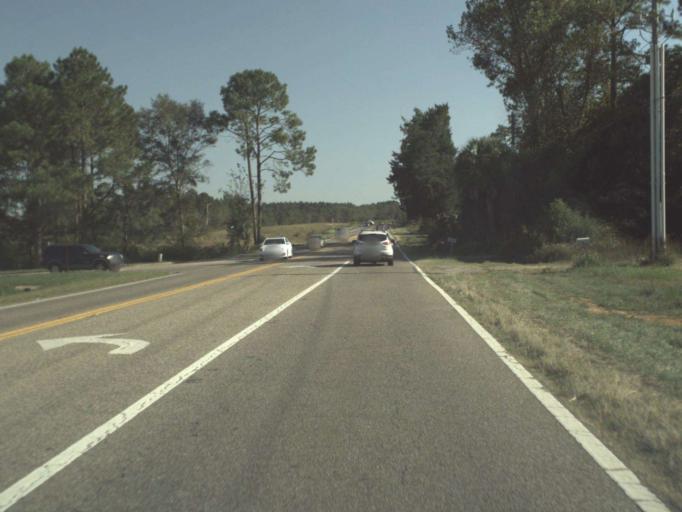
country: US
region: Florida
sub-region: Walton County
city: DeFuniak Springs
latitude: 30.6592
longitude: -86.1195
